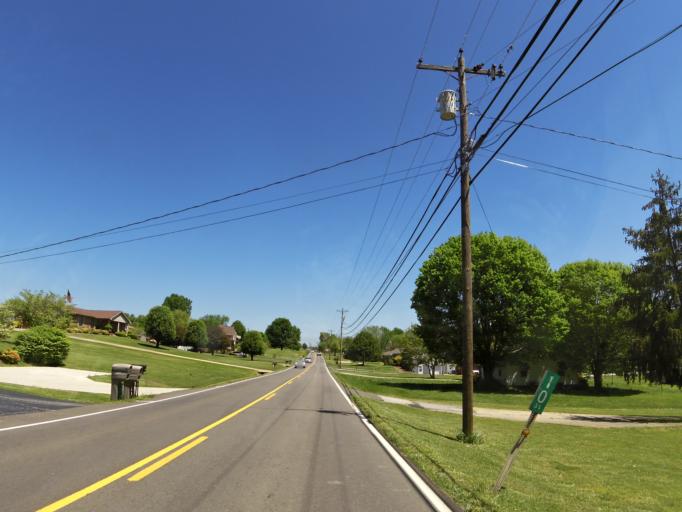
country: US
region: Tennessee
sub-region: Greene County
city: Greeneville
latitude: 36.1357
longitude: -82.8801
